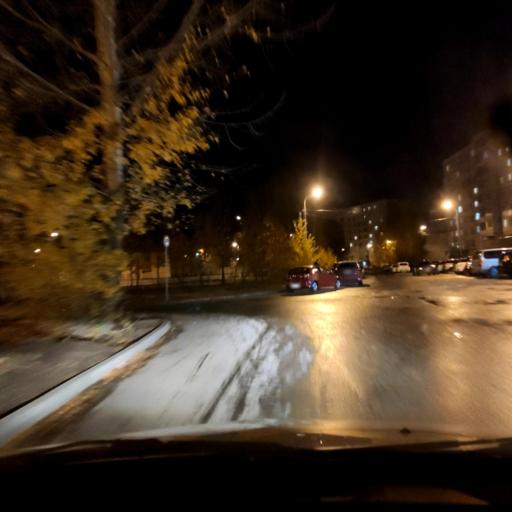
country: RU
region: Bashkortostan
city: Ufa
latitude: 54.7680
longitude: 56.0793
